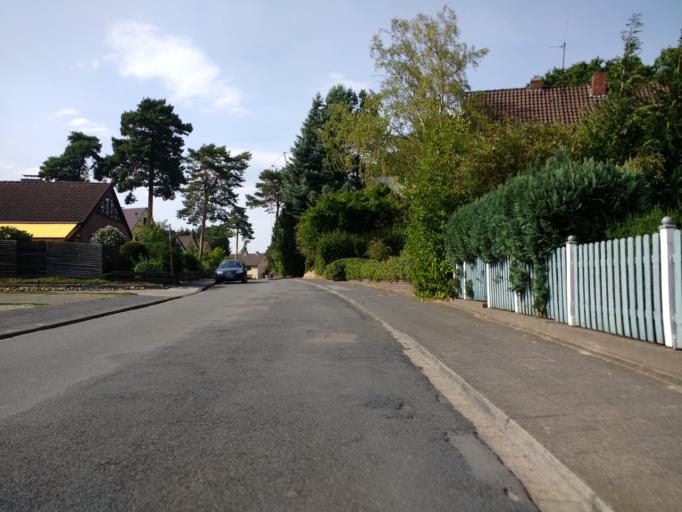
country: DE
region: Lower Saxony
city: Gifhorn
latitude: 52.4747
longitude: 10.5468
